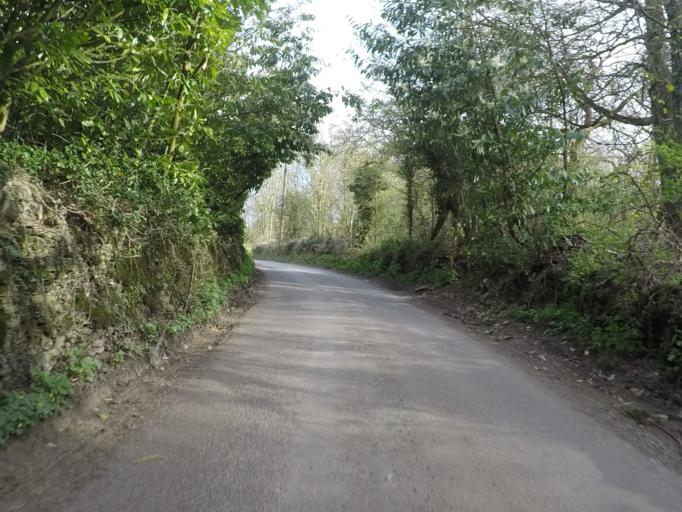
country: GB
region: England
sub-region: Oxfordshire
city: North Leigh
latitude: 51.8398
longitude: -1.4617
